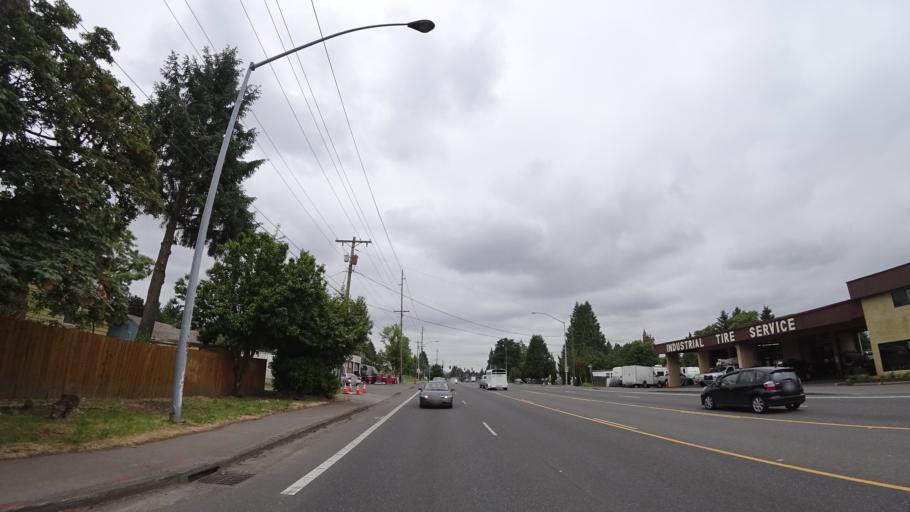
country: US
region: Oregon
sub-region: Multnomah County
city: Lents
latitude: 45.5626
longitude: -122.5867
